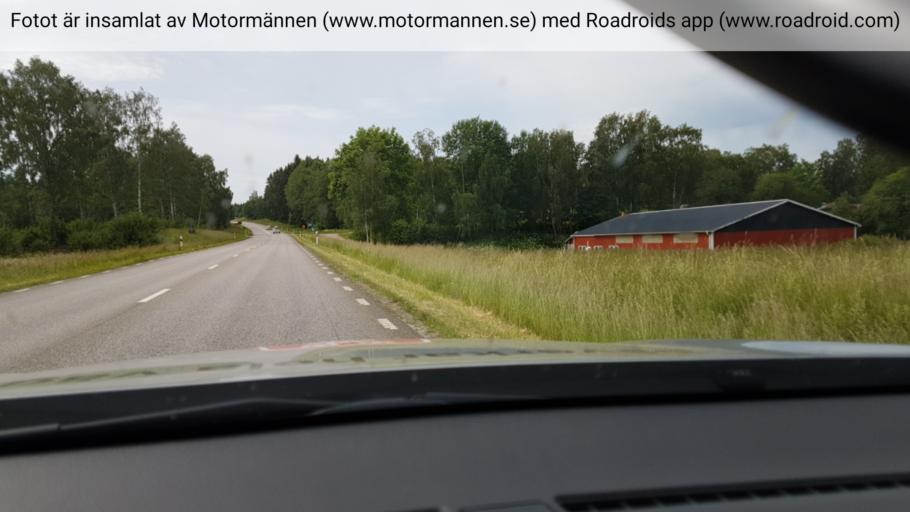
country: SE
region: Vaestra Goetaland
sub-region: Falkopings Kommun
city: Akarp
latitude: 58.2231
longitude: 13.6499
